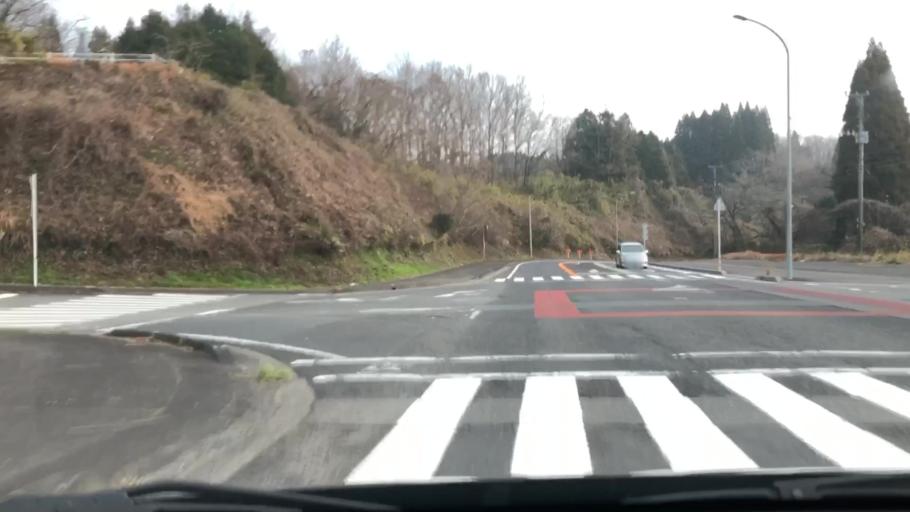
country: JP
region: Oita
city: Takedamachi
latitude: 32.9728
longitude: 131.5191
